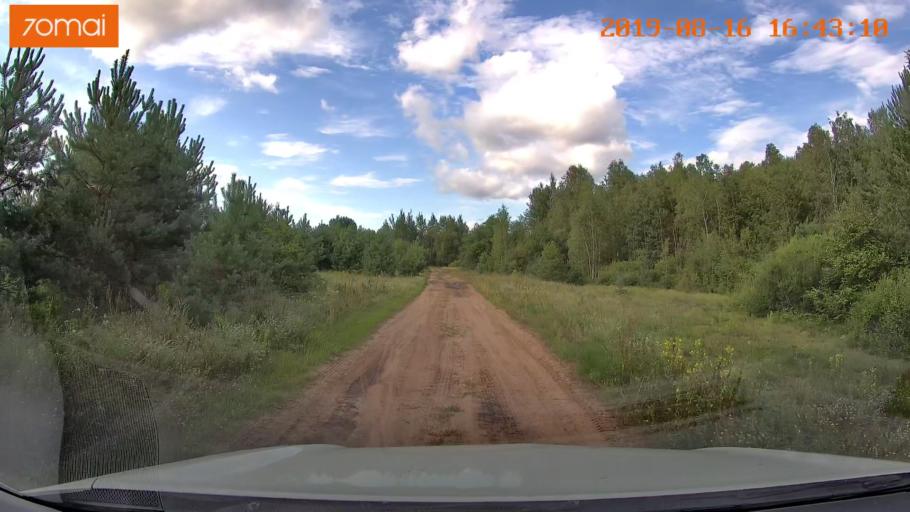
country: BY
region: Mogilev
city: Asipovichy
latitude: 53.2432
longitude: 28.7776
